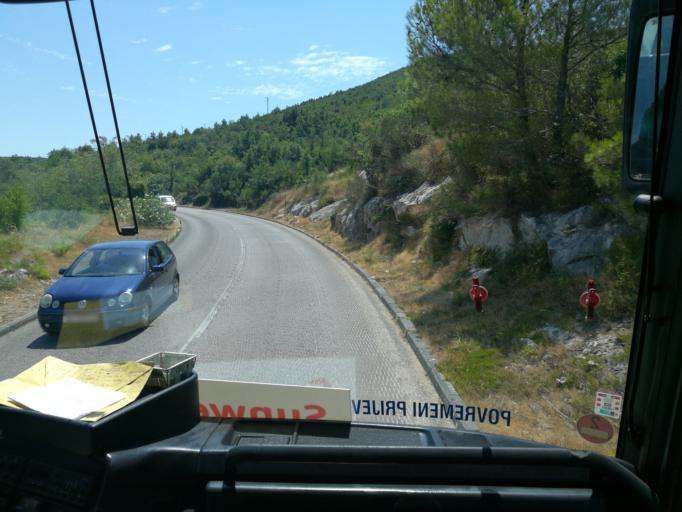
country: HR
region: Dubrovacko-Neretvanska
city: Cavtat
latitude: 42.5786
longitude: 18.2311
